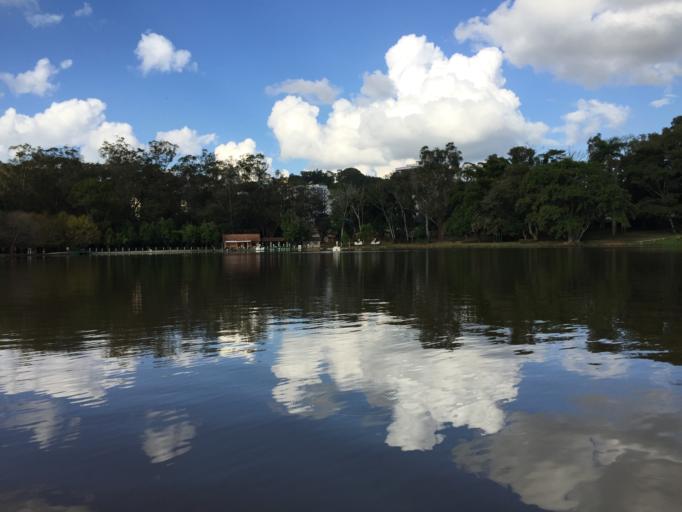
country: BR
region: Minas Gerais
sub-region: Caxambu
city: Caxambu
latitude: -21.9844
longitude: -44.9389
